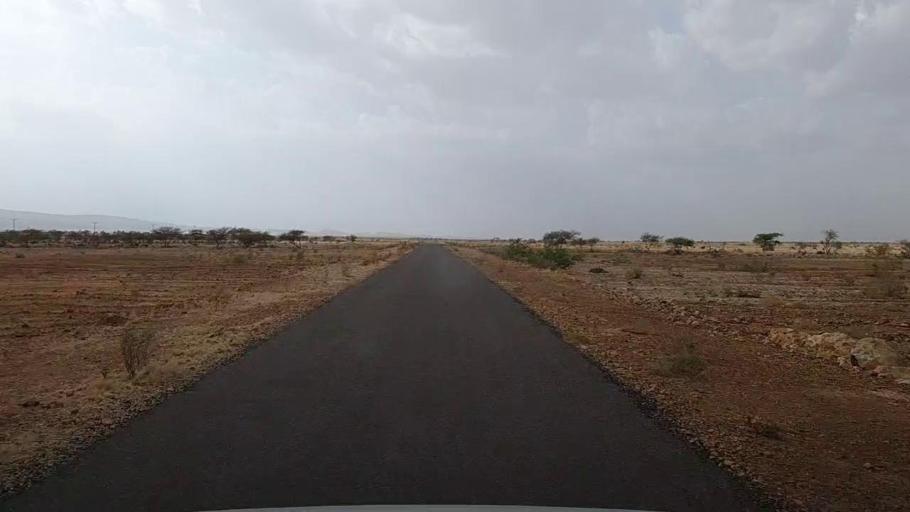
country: PK
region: Sindh
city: Jamshoro
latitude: 25.4390
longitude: 67.6841
